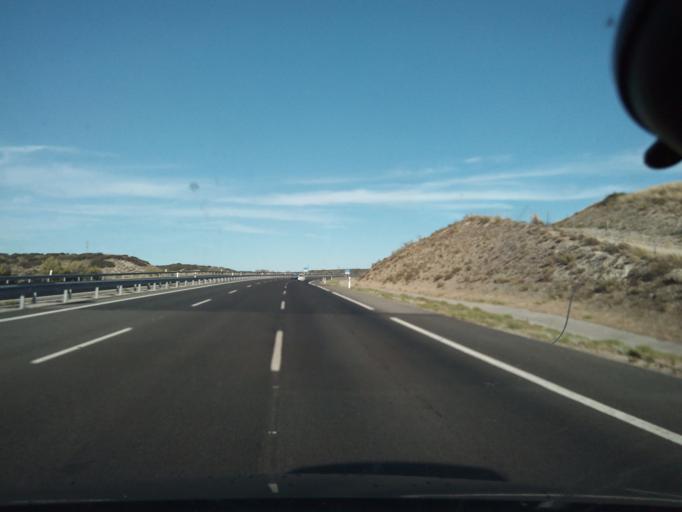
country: ES
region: Madrid
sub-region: Provincia de Madrid
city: Aranjuez
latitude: 40.0104
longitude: -3.6231
